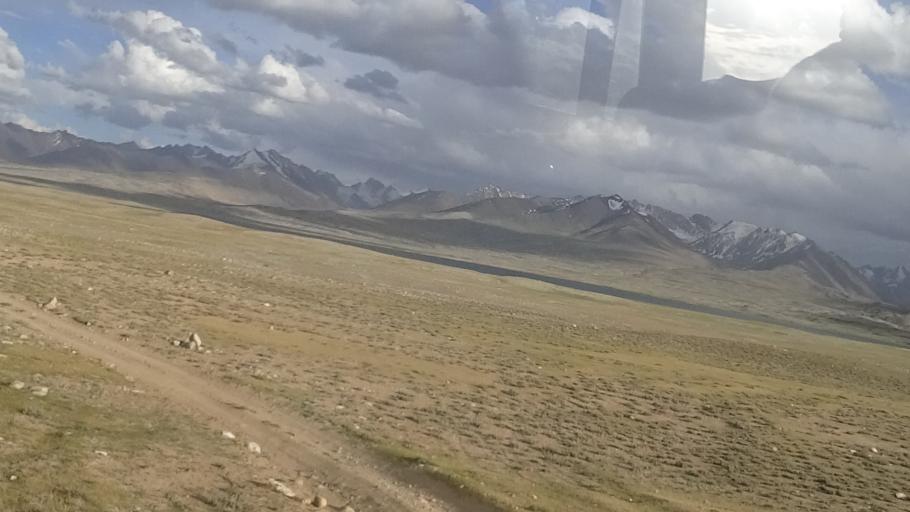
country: TJ
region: Gorno-Badakhshan
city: Murghob
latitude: 37.4623
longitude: 73.6162
